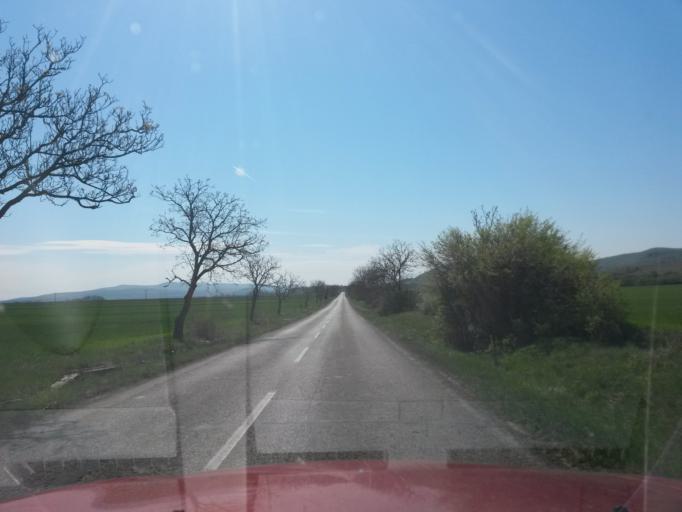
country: HU
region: Borsod-Abauj-Zemplen
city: Satoraljaujhely
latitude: 48.5395
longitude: 21.5699
